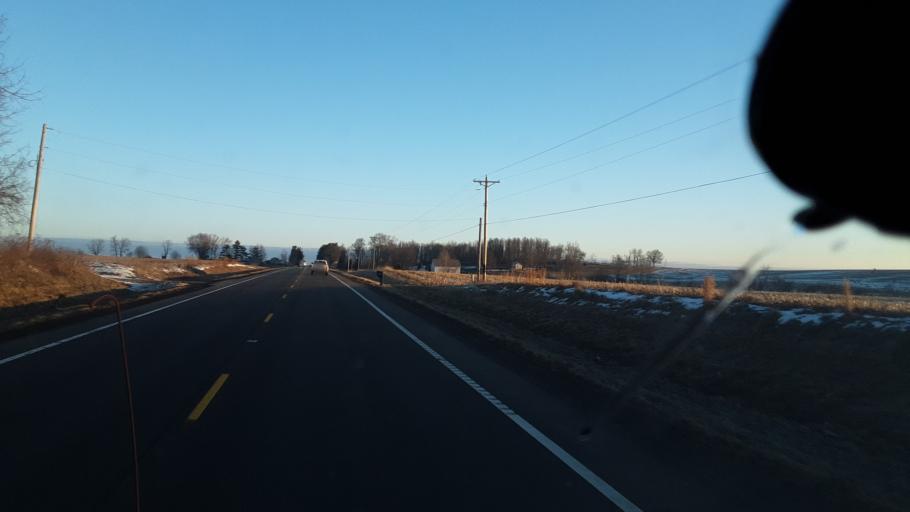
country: US
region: Ohio
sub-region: Perry County
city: Thornport
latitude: 39.8504
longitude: -82.3952
